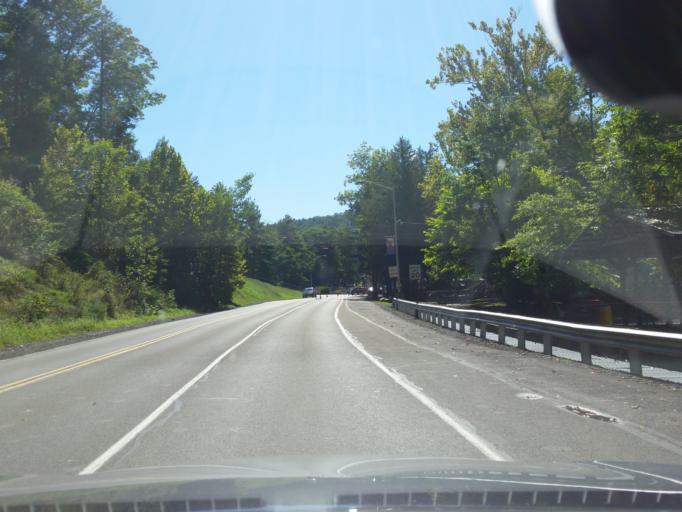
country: US
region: Pennsylvania
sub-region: Northumberland County
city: Elysburg
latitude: 40.8809
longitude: -76.5037
